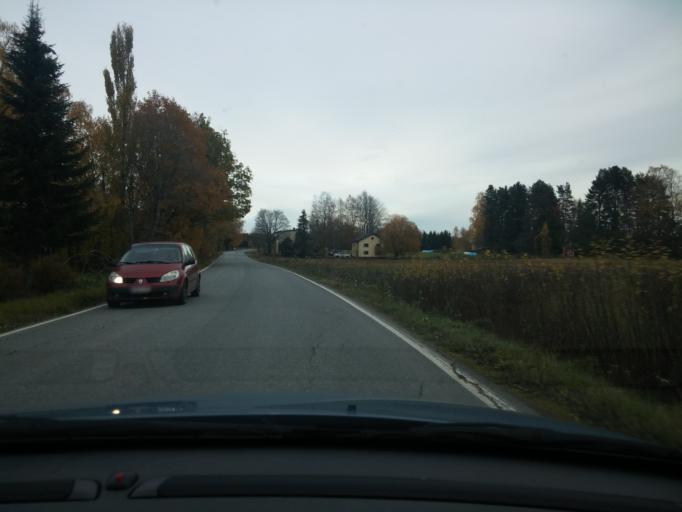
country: FI
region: Haeme
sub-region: Forssa
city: Tammela
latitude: 60.7674
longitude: 23.8460
